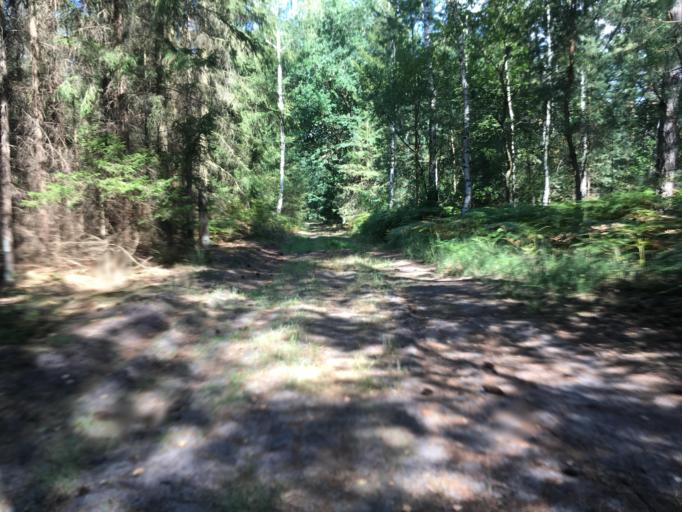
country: DE
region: Brandenburg
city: Zehdenick
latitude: 52.9976
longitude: 13.3764
